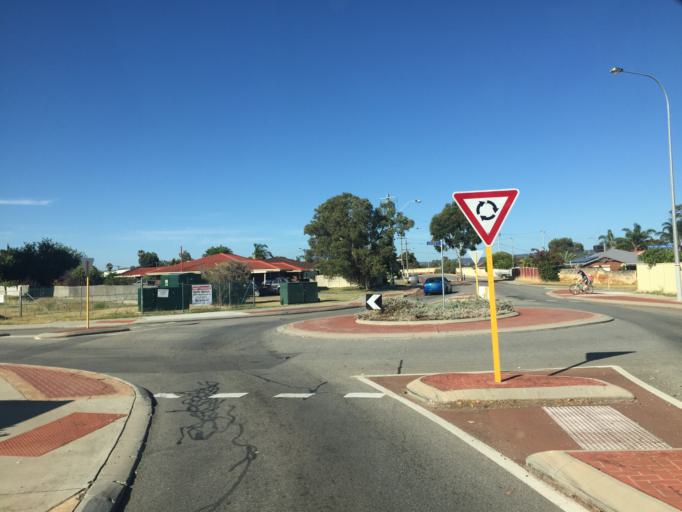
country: AU
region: Western Australia
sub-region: Canning
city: East Cannington
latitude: -32.0092
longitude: 115.9705
